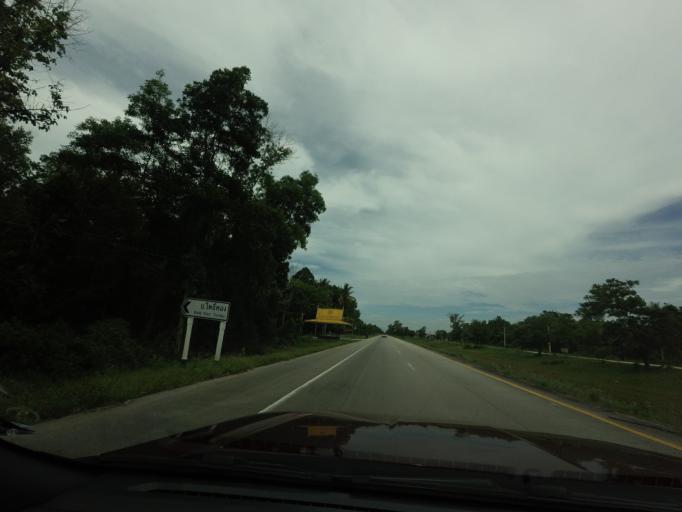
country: TH
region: Narathiwat
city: Narathiwat
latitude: 6.3576
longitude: 101.9072
